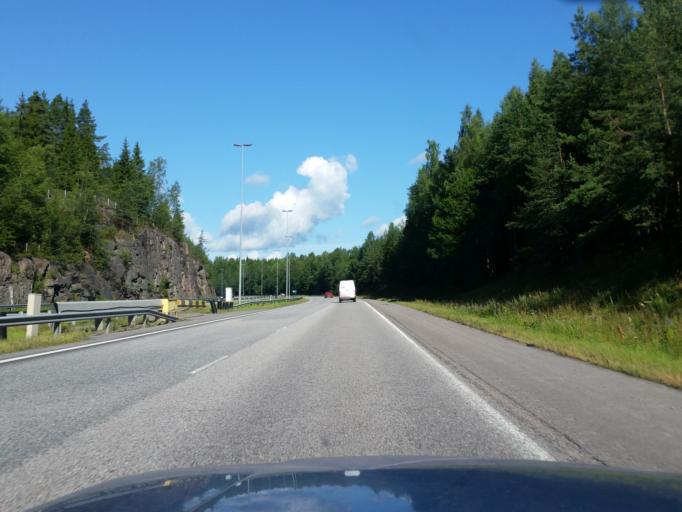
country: FI
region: Uusimaa
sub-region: Helsinki
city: Vihti
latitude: 60.2868
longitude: 24.4176
